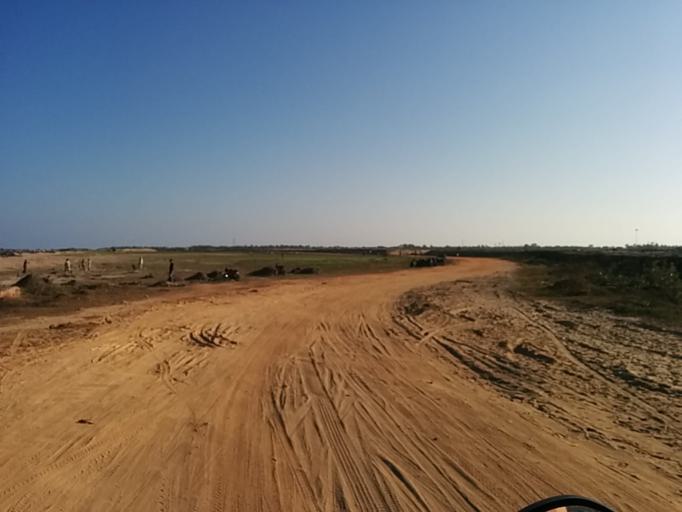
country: IN
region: Pondicherry
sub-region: Puducherry
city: Puducherry
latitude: 11.9118
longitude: 79.8295
